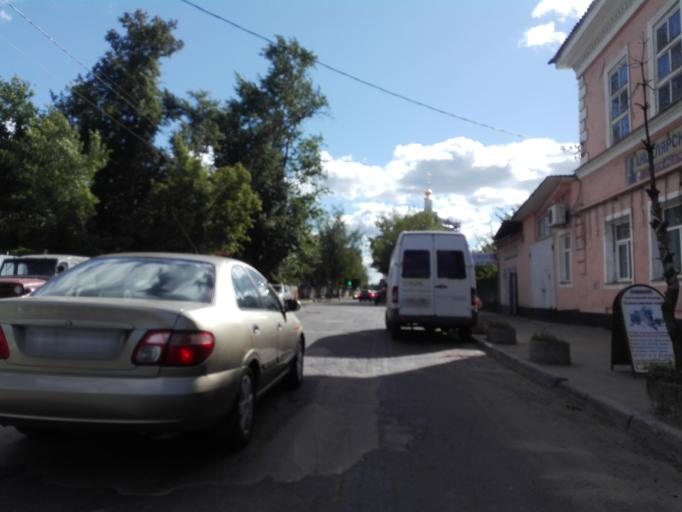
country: RU
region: Orjol
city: Orel
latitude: 52.9604
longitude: 36.0607
